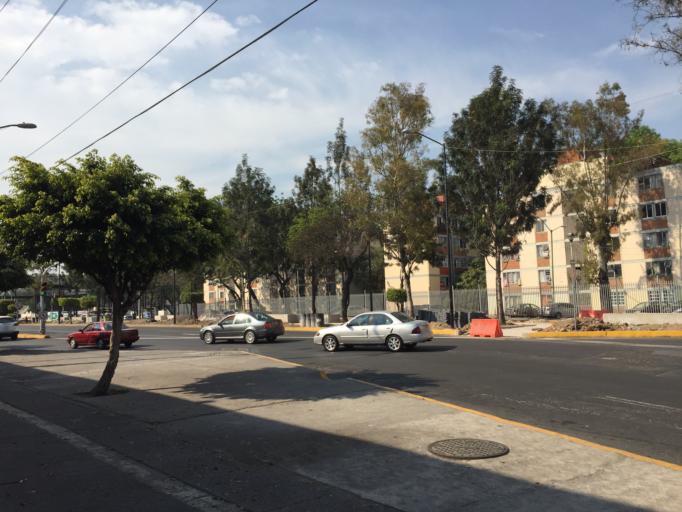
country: MX
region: Mexico
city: Colonia Lindavista
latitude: 19.5025
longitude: -99.1300
